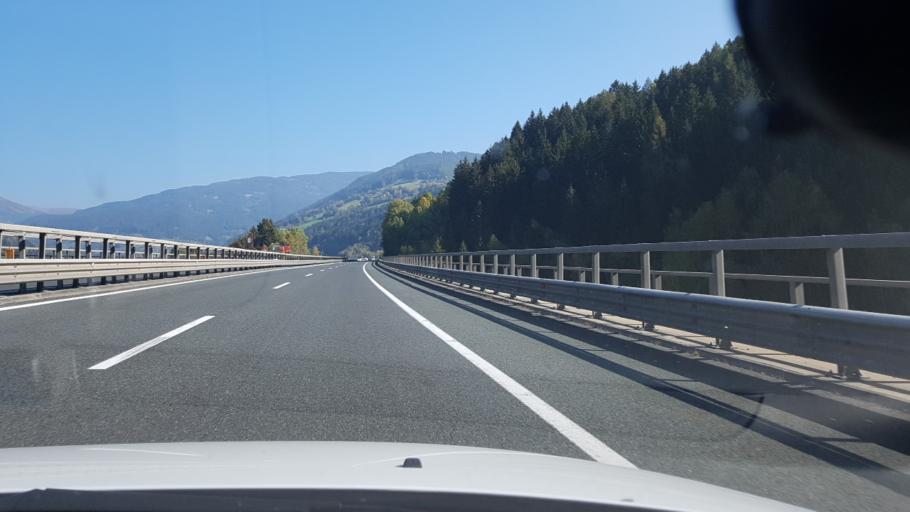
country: AT
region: Carinthia
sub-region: Politischer Bezirk Spittal an der Drau
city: Gmuend
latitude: 46.9179
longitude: 13.5674
